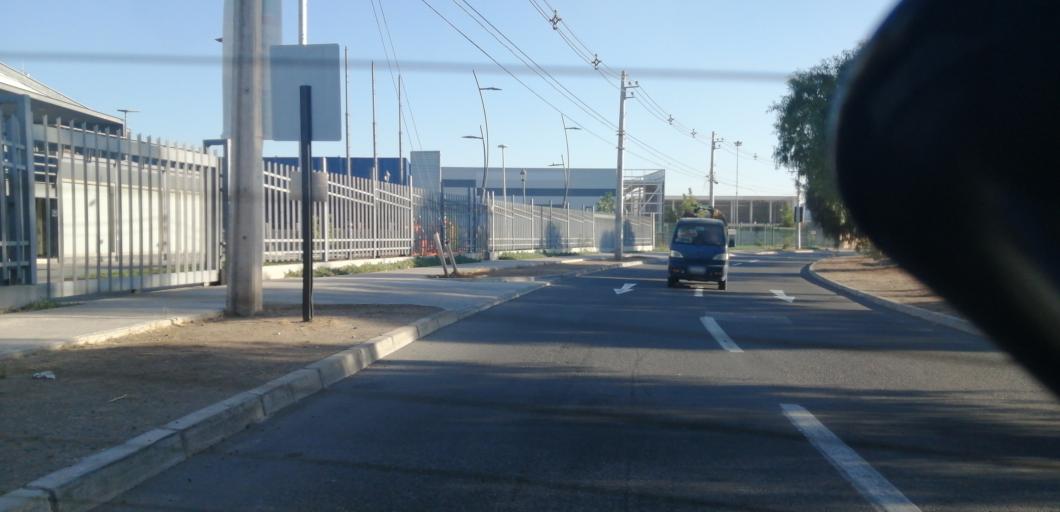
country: CL
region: Santiago Metropolitan
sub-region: Provincia de Santiago
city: Lo Prado
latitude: -33.4510
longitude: -70.8503
